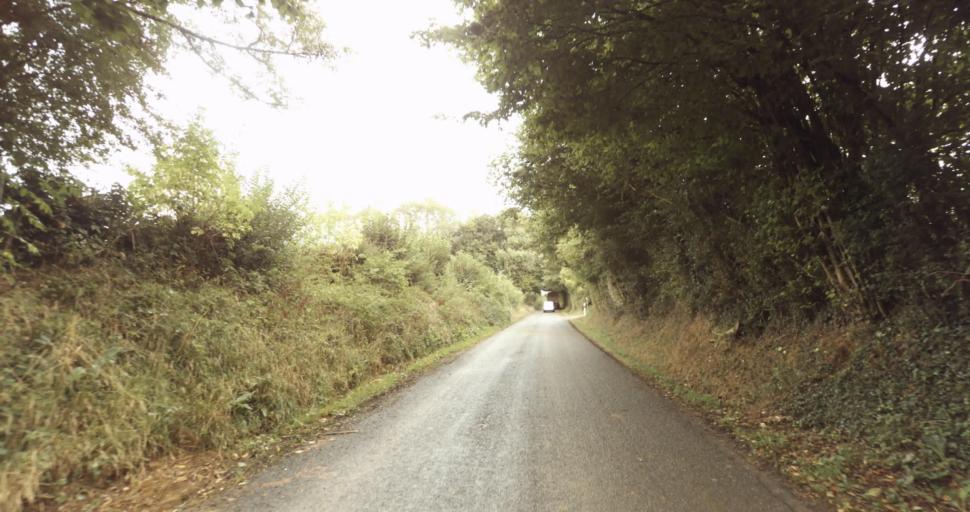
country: FR
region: Lower Normandy
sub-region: Departement de l'Orne
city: Vimoutiers
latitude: 48.8557
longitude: 0.2250
